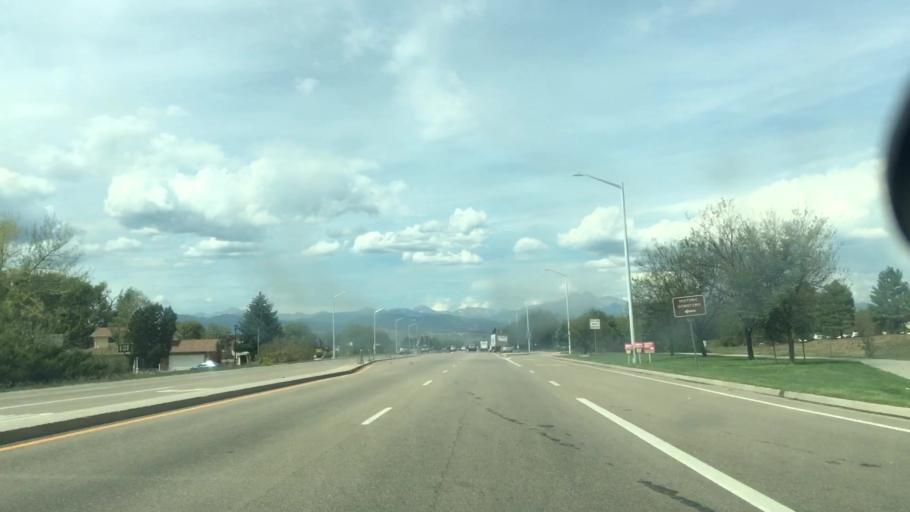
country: US
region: Colorado
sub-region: Boulder County
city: Longmont
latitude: 40.2033
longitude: -105.0981
